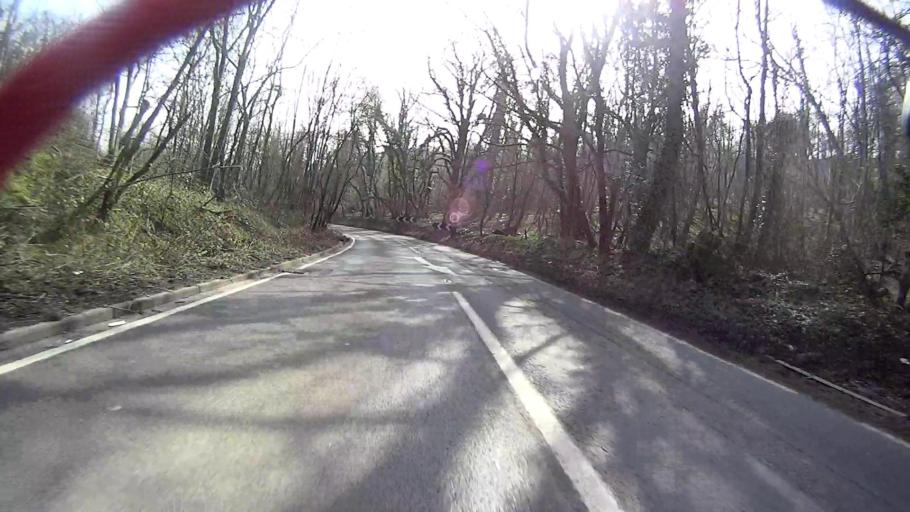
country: GB
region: England
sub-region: Surrey
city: Headley
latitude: 51.2611
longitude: -0.2643
